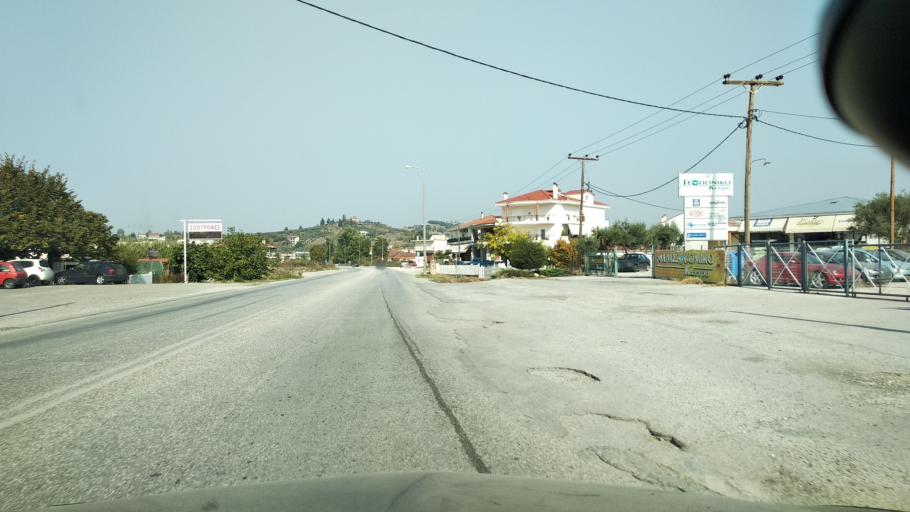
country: GR
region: Thessaly
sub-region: Trikala
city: Trikala
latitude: 39.5630
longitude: 21.7811
